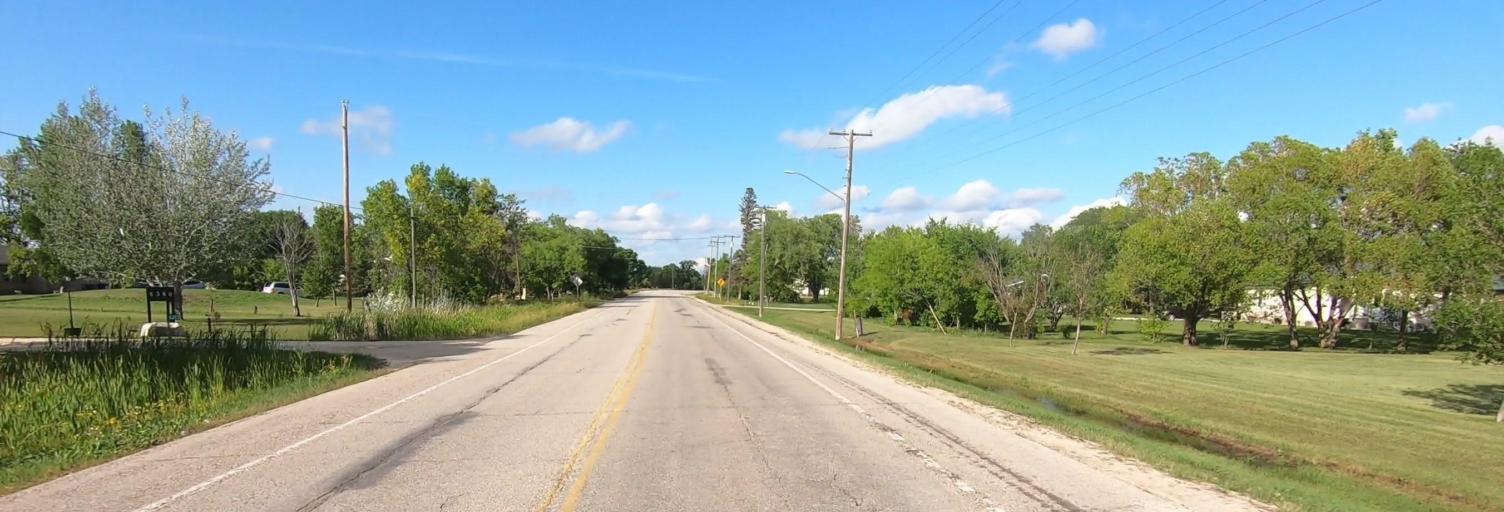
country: CA
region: Manitoba
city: Selkirk
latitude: 50.0680
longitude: -96.9487
